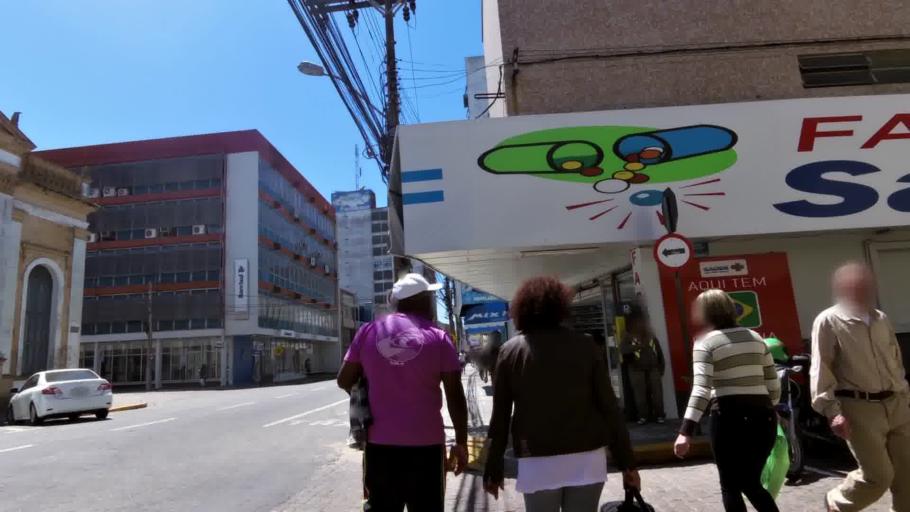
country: BR
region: Rio Grande do Sul
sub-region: Rio Grande
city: Rio Grande
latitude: -32.0311
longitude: -52.0947
